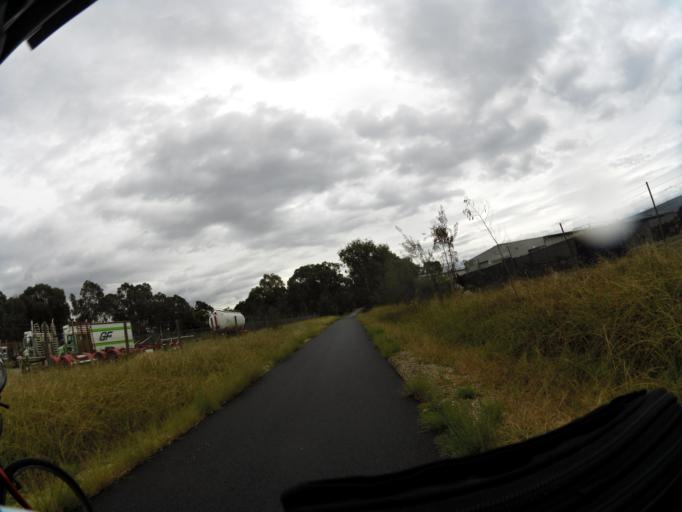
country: AU
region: Victoria
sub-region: Wodonga
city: Wodonga
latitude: -36.1352
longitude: 146.9021
